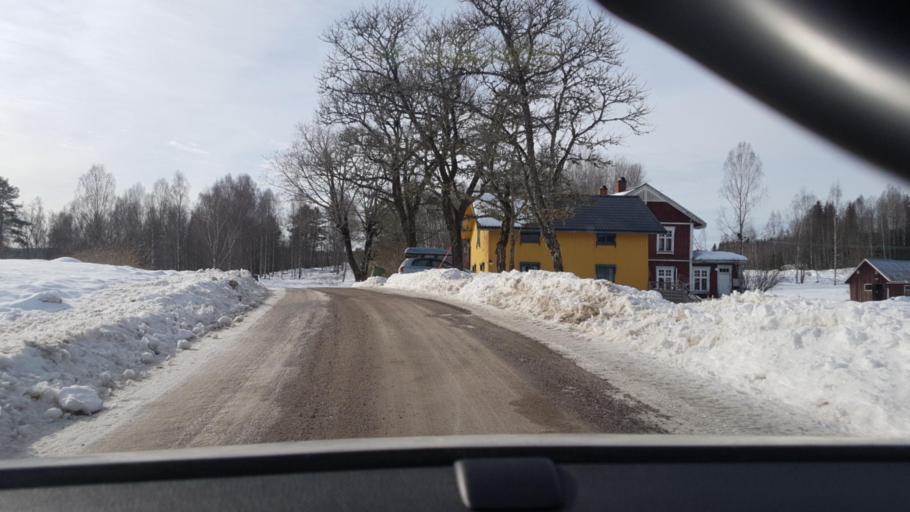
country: NO
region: Ostfold
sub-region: Romskog
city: Romskog
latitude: 59.8405
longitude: 11.9623
